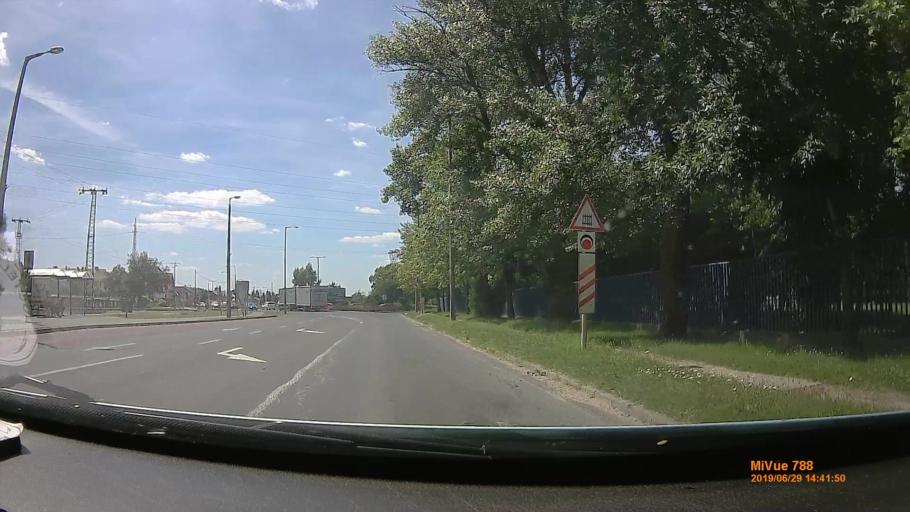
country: HU
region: Komarom-Esztergom
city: Nyergesujfalu
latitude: 47.7586
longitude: 18.5699
